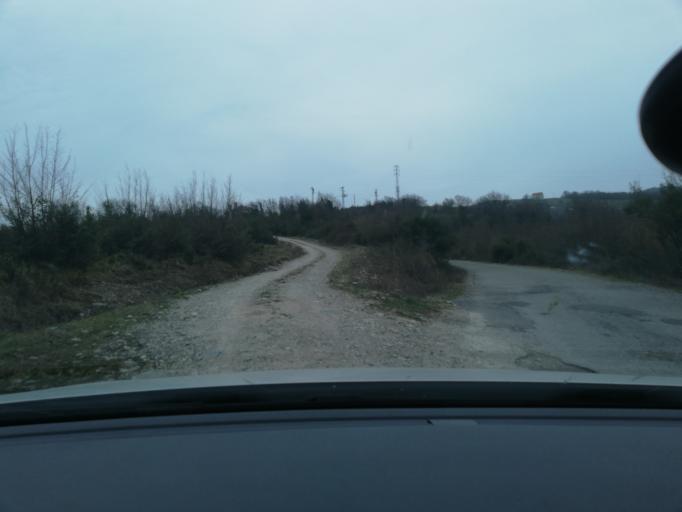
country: TR
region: Zonguldak
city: Saltukova
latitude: 41.5188
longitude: 32.0776
